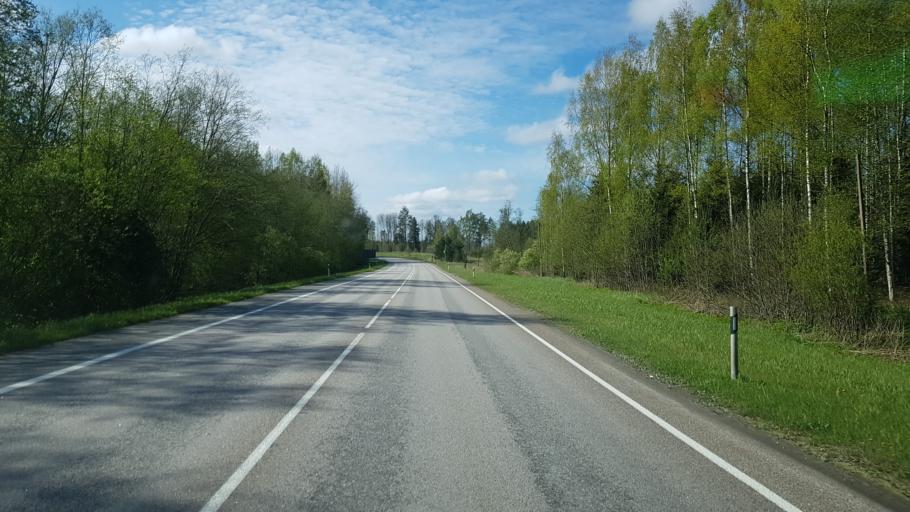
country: EE
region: Valgamaa
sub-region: Valga linn
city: Valga
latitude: 57.8684
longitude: 26.0592
